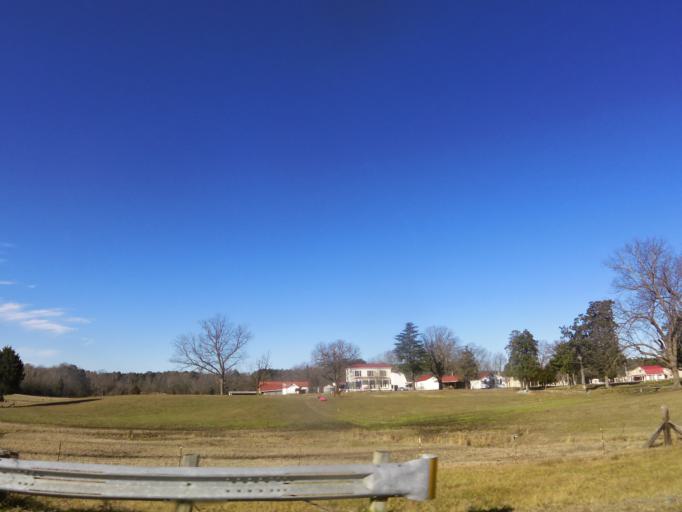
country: US
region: Virginia
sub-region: City of Petersburg
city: Petersburg
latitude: 37.1904
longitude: -77.4227
